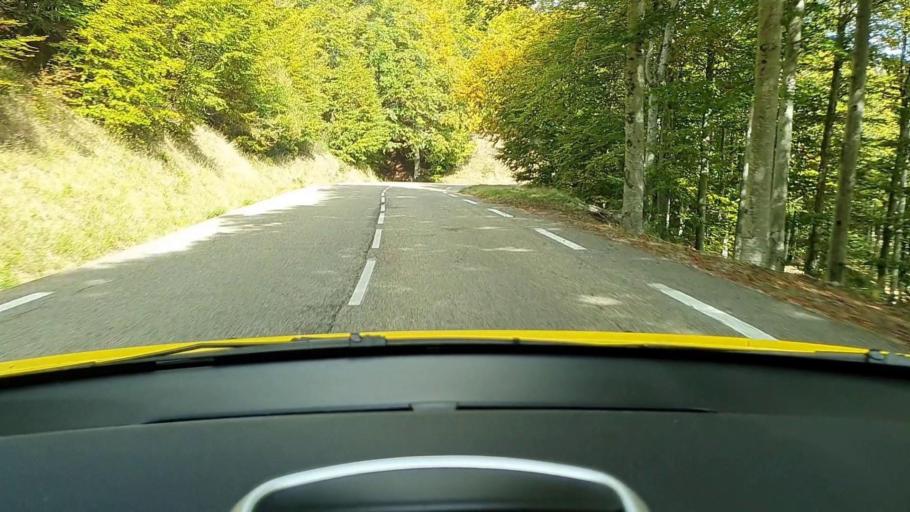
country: FR
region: Languedoc-Roussillon
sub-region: Departement du Gard
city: Valleraugue
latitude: 44.1087
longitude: 3.5462
